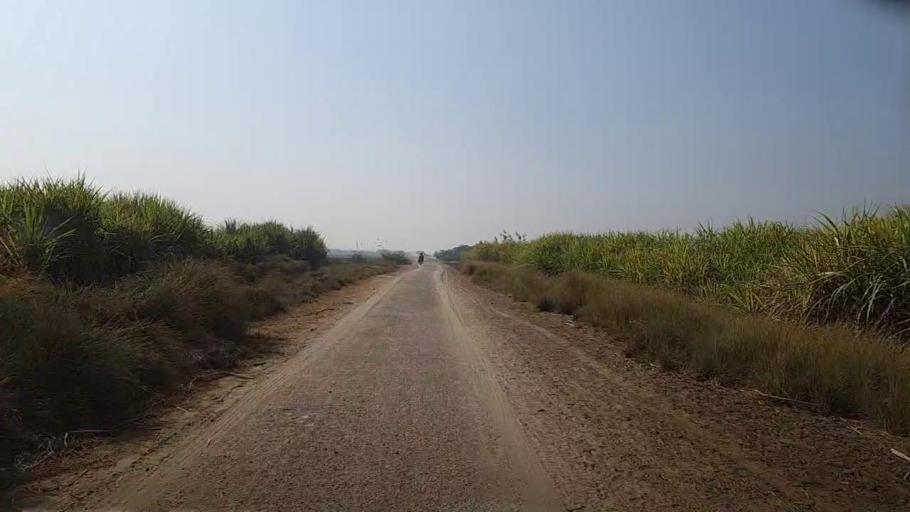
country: PK
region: Sindh
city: Bozdar
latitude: 27.2600
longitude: 68.6186
